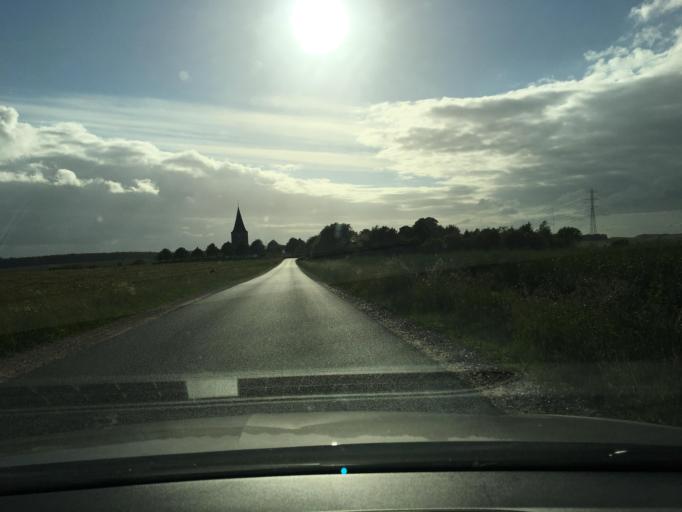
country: DK
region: Central Jutland
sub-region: Favrskov Kommune
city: Hinnerup
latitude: 56.2794
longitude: 10.0481
